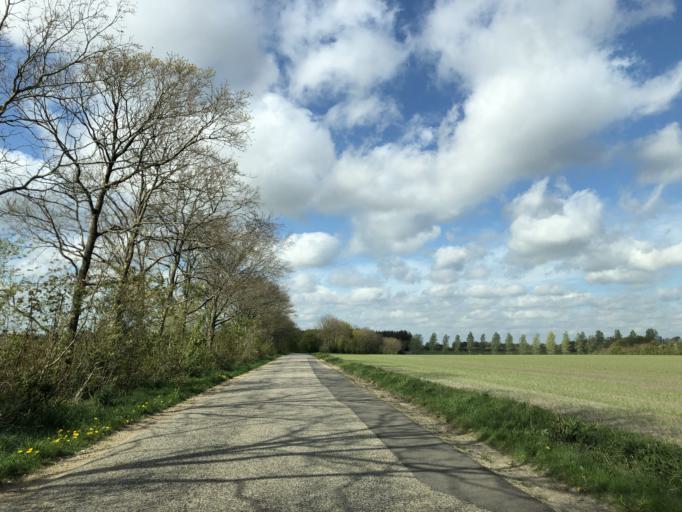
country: DK
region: Central Jutland
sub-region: Herning Kommune
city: Avlum
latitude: 56.2923
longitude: 8.6987
